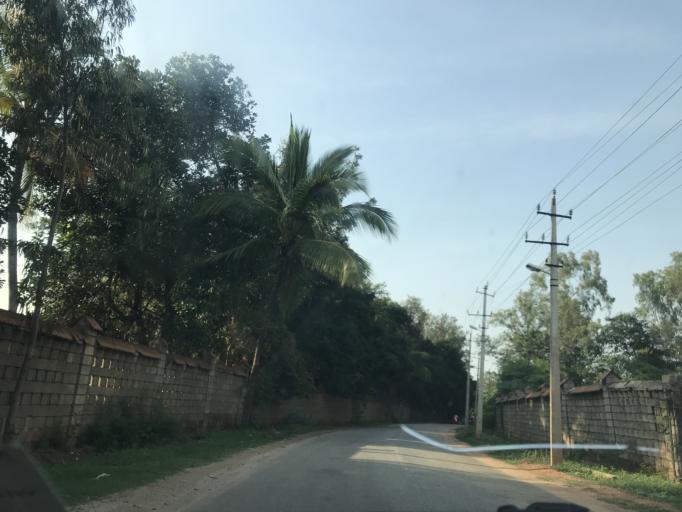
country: IN
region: Karnataka
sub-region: Bangalore Rural
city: Devanhalli
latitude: 13.2027
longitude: 77.6451
